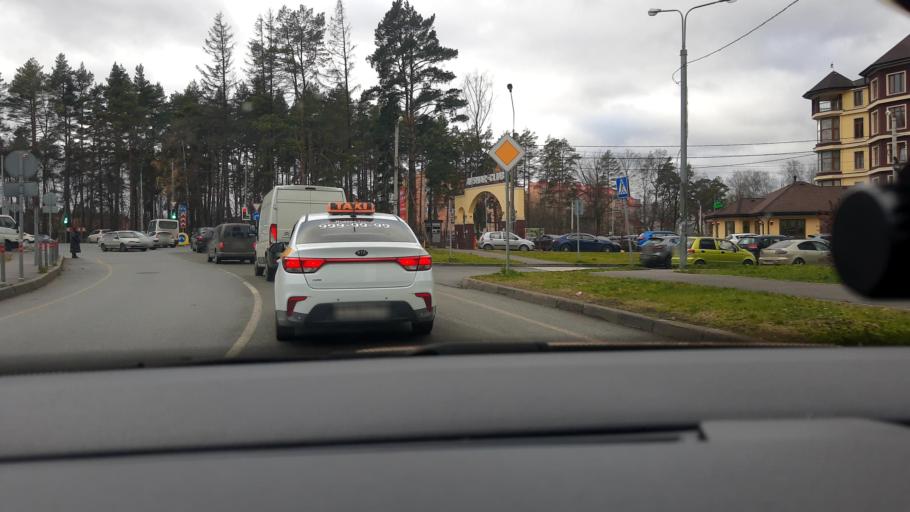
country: RU
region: Moskovskaya
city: Opalikha
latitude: 55.8362
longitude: 37.2656
